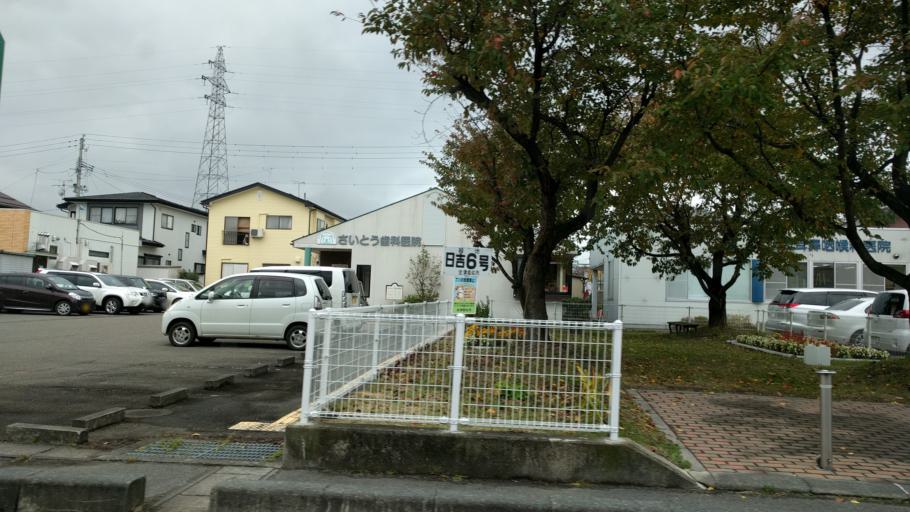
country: JP
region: Fukushima
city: Kitakata
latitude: 37.4769
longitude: 139.9110
